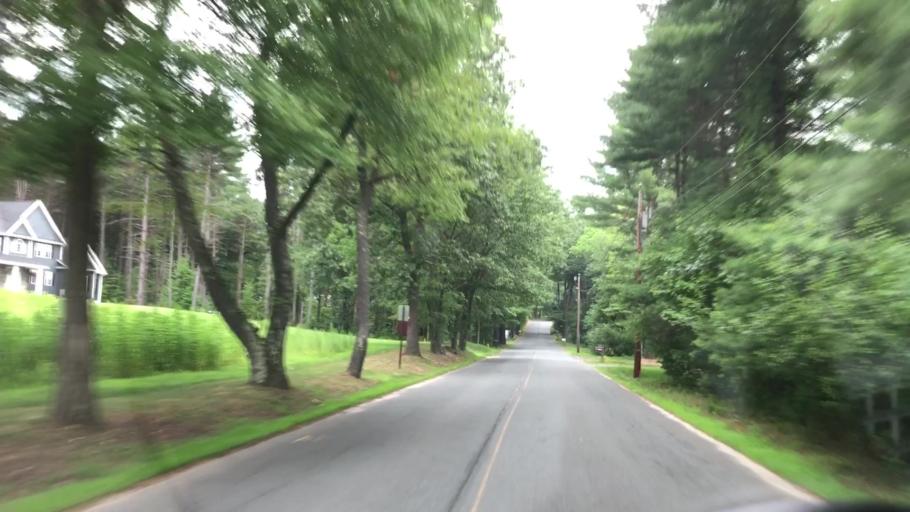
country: US
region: Massachusetts
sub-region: Hampshire County
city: Southampton
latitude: 42.2220
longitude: -72.6859
